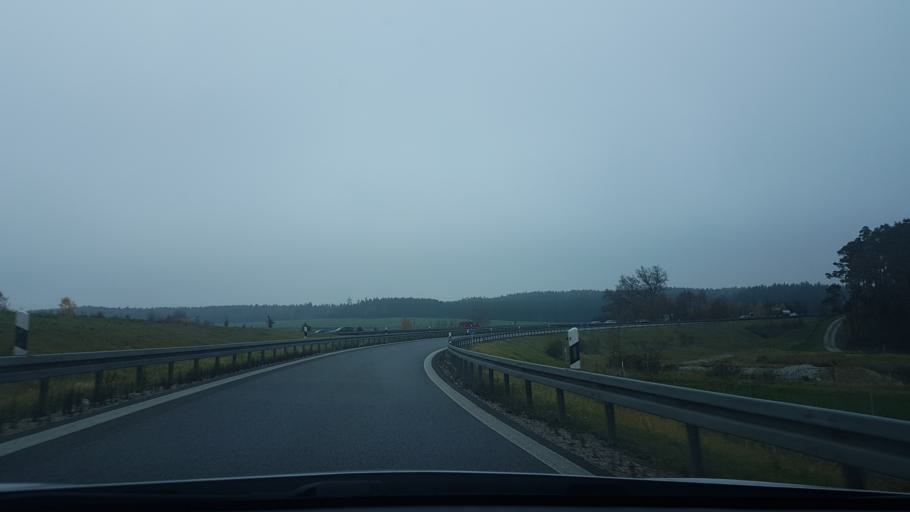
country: DE
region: Bavaria
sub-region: Lower Bavaria
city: Bad Abbach
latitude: 48.8897
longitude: 12.0767
